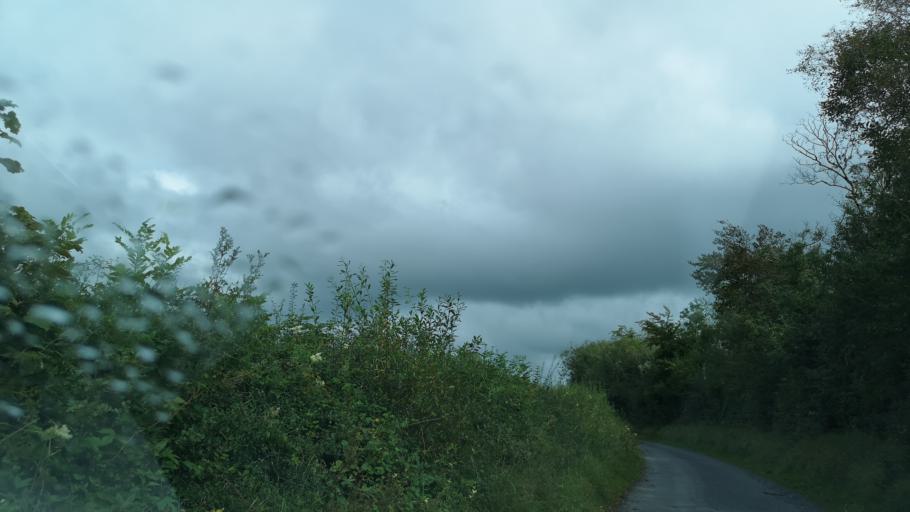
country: IE
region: Connaught
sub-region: County Galway
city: Loughrea
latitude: 53.3061
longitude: -8.6036
